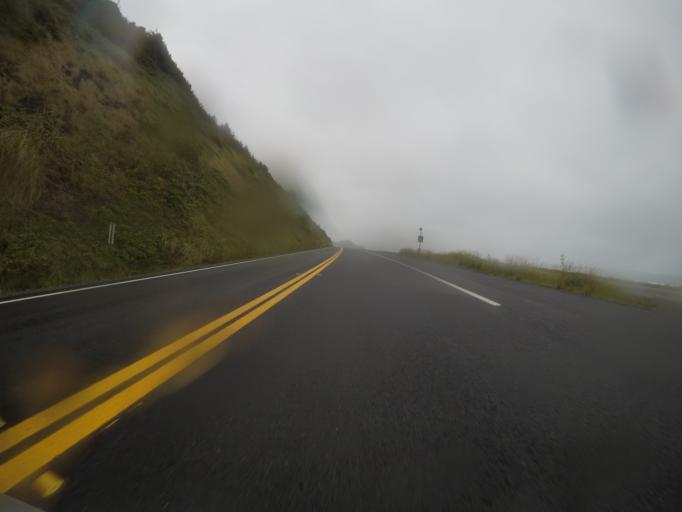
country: US
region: California
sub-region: Humboldt County
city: Westhaven-Moonstone
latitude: 41.2813
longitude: -124.0931
